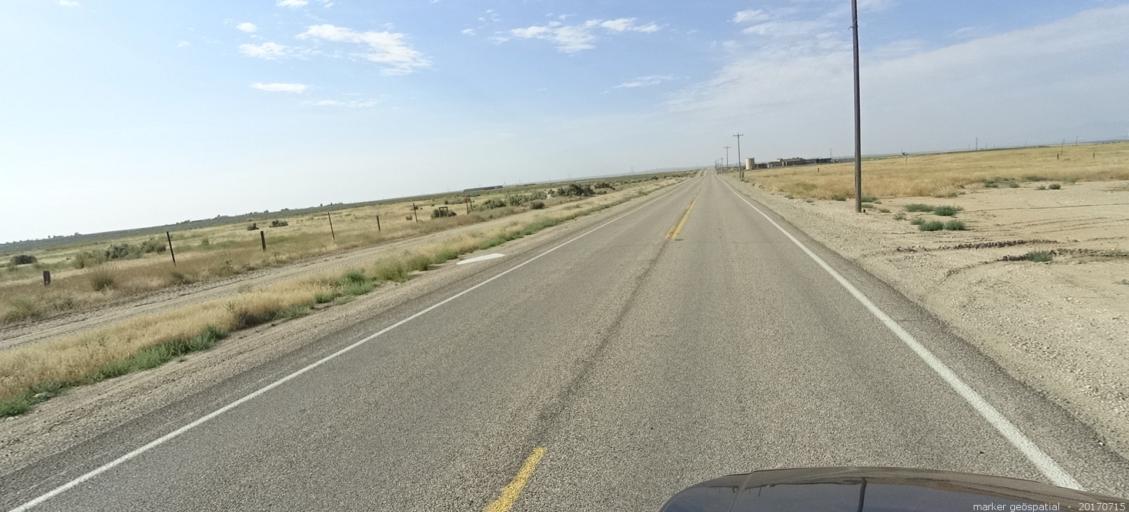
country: US
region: Idaho
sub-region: Ada County
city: Boise
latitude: 43.4685
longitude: -116.2343
